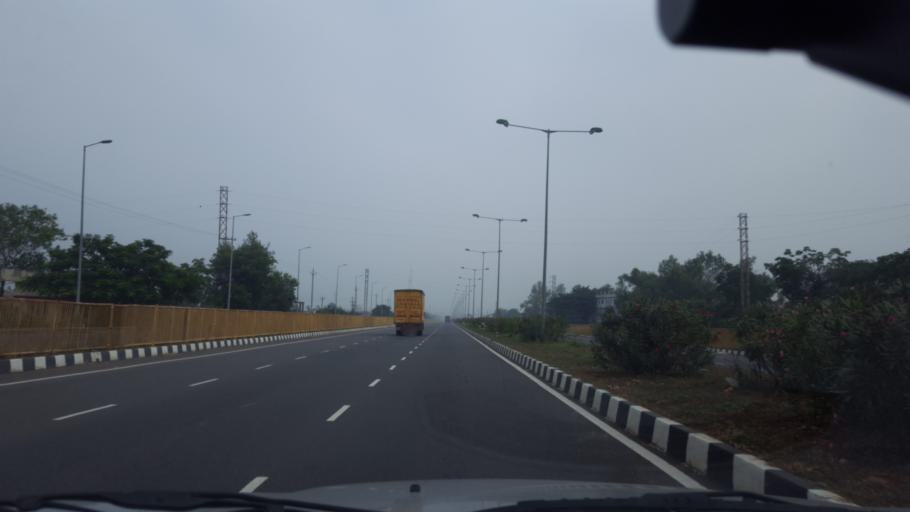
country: IN
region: Andhra Pradesh
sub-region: Prakasam
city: pedda nakkalapalem
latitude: 15.9671
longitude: 80.0940
